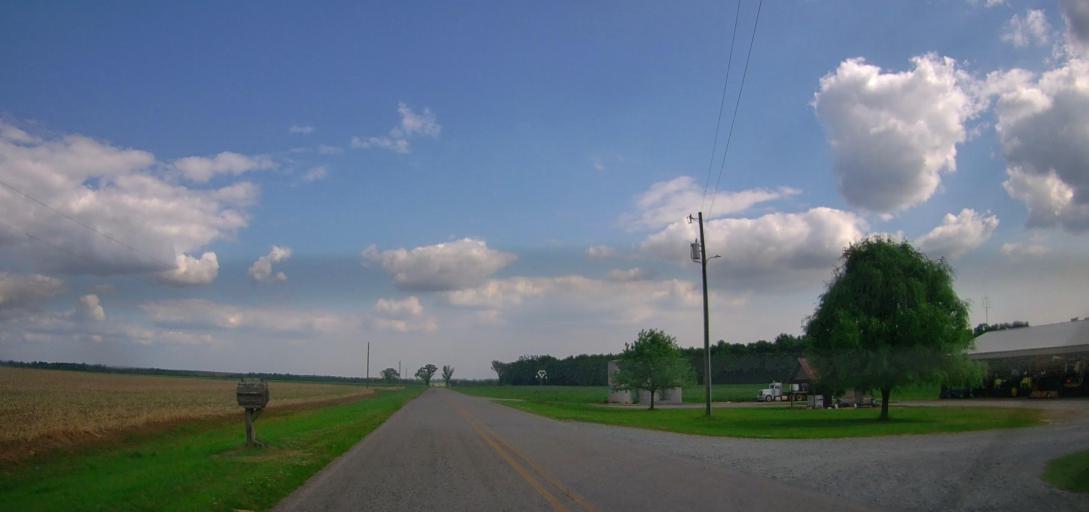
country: US
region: Georgia
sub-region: Laurens County
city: East Dublin
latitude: 32.6868
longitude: -82.8955
